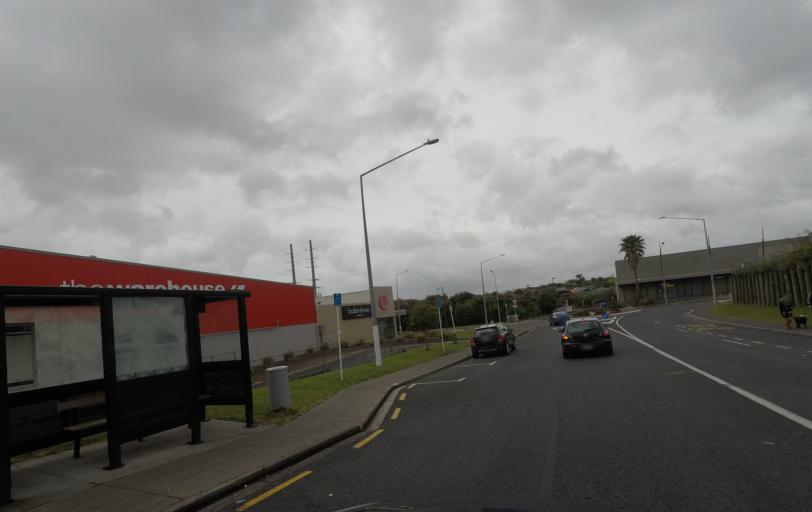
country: NZ
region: Auckland
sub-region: Auckland
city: Rosebank
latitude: -36.8224
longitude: 174.6109
